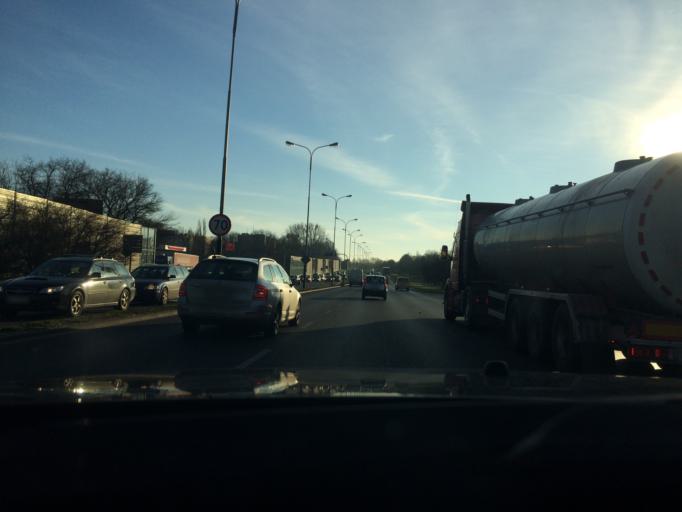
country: PL
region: Lodz Voivodeship
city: Lodz
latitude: 51.7364
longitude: 19.4420
